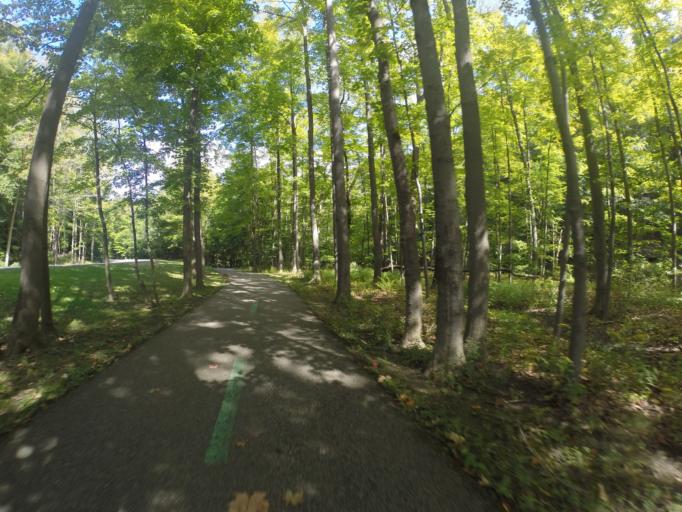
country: US
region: Ohio
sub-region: Cuyahoga County
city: Richmond Heights
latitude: 41.5503
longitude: -81.5292
